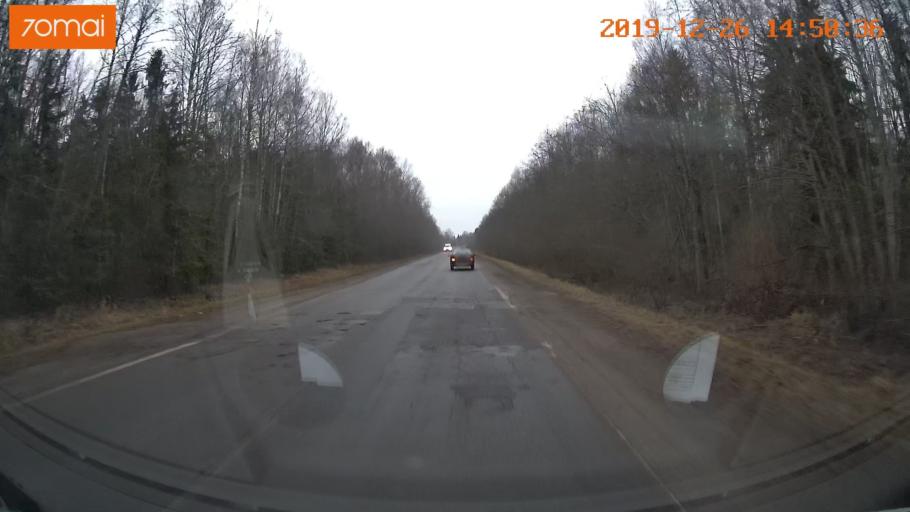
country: RU
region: Jaroslavl
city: Poshekhon'ye
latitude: 58.3308
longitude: 38.9230
